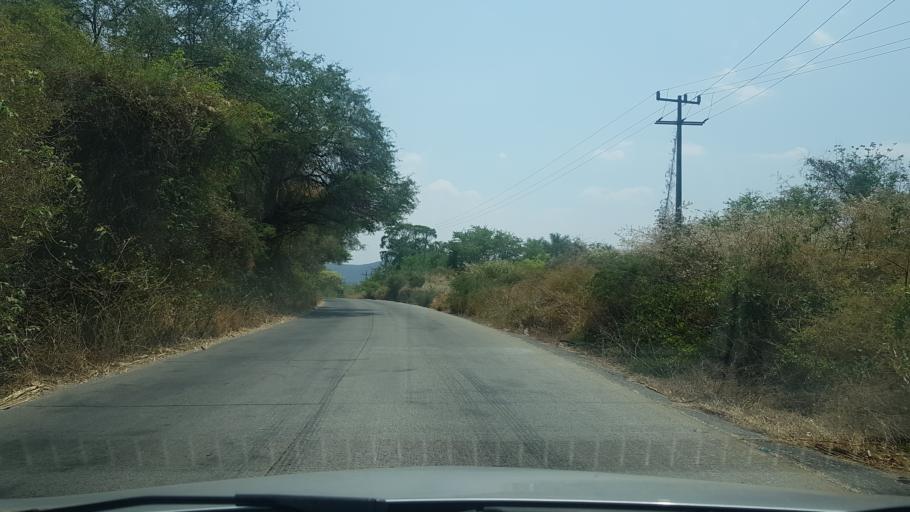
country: MX
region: Morelos
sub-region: Tlaltizapan de Zapata
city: Colonia Palo Prieto (Chipitongo)
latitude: 18.7535
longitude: -99.1130
